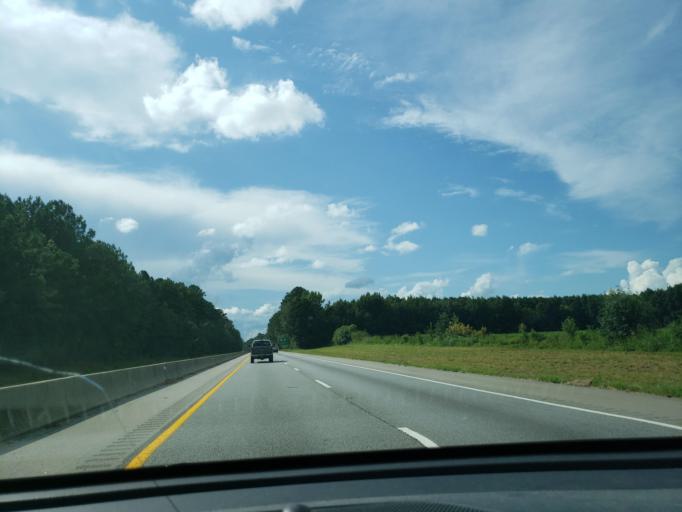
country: US
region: Virginia
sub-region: City of Franklin
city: Franklin
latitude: 36.6555
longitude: -76.9274
